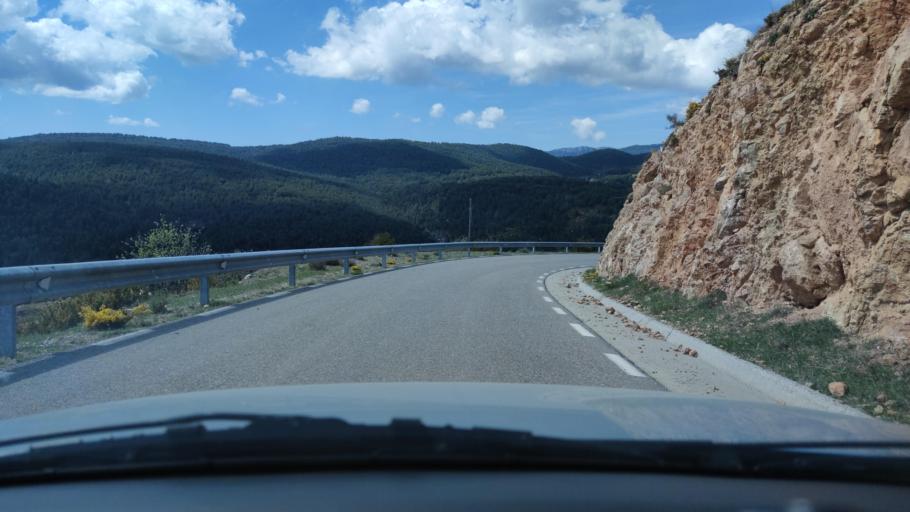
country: ES
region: Catalonia
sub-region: Provincia de Lleida
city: Coll de Nargo
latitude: 42.2822
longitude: 1.2307
